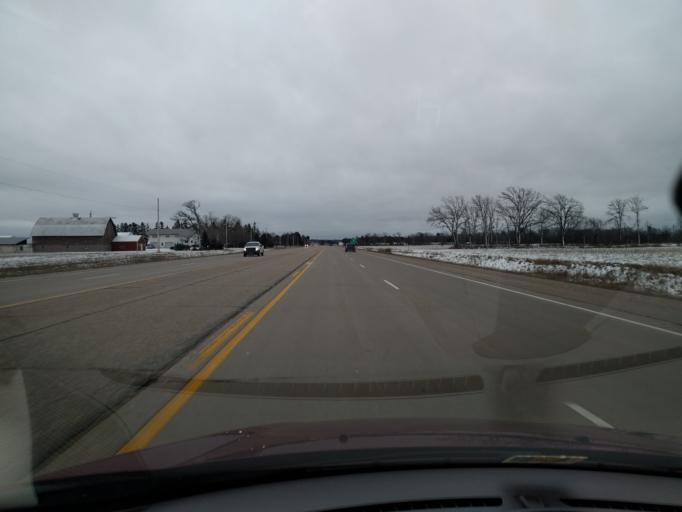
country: US
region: Wisconsin
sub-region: Portage County
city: Whiting
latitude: 44.5228
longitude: -89.4787
